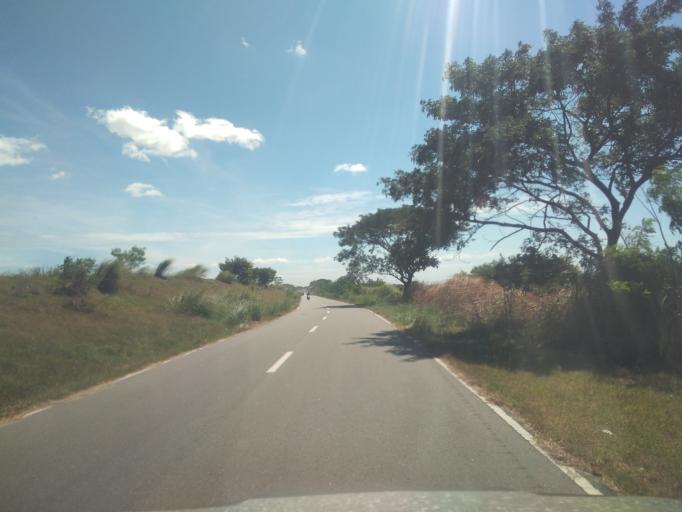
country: PH
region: Central Luzon
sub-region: Province of Pampanga
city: San Basilio
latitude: 15.0221
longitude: 120.6014
